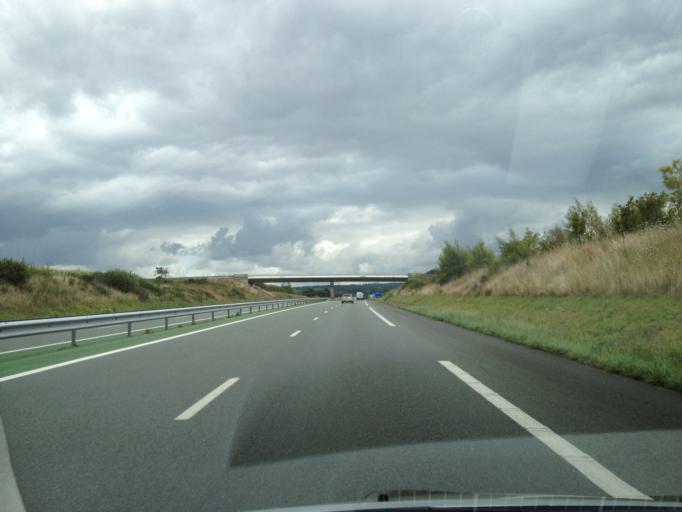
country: FR
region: Pays de la Loire
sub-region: Departement de la Vendee
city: Beaurepaire
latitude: 46.8957
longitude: -1.0812
